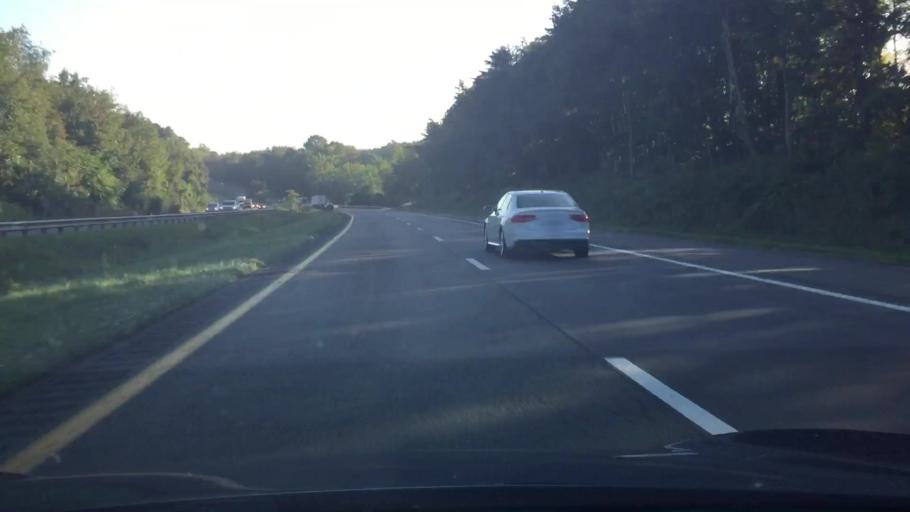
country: US
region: Virginia
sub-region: Pulaski County
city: Pulaski
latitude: 37.0436
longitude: -80.7193
